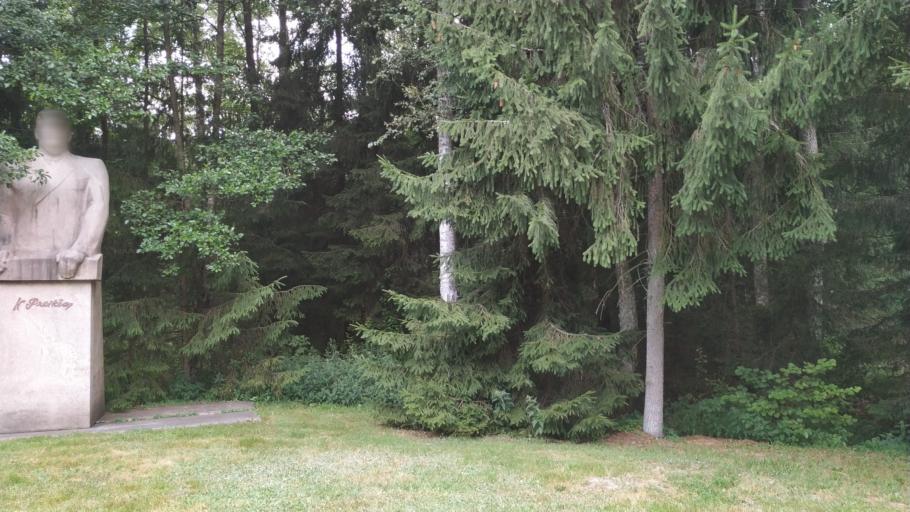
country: LT
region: Alytaus apskritis
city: Druskininkai
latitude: 54.0209
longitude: 24.0805
